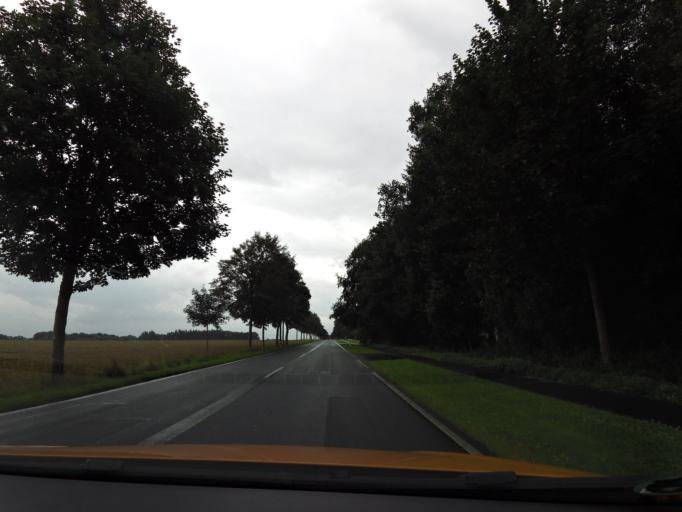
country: DE
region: Lower Saxony
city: Bassum
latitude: 52.8269
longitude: 8.7391
